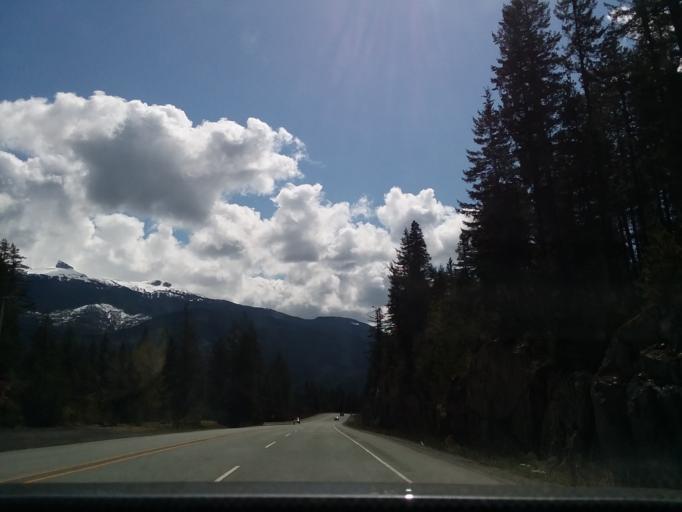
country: CA
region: British Columbia
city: Whistler
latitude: 50.0320
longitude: -123.1227
